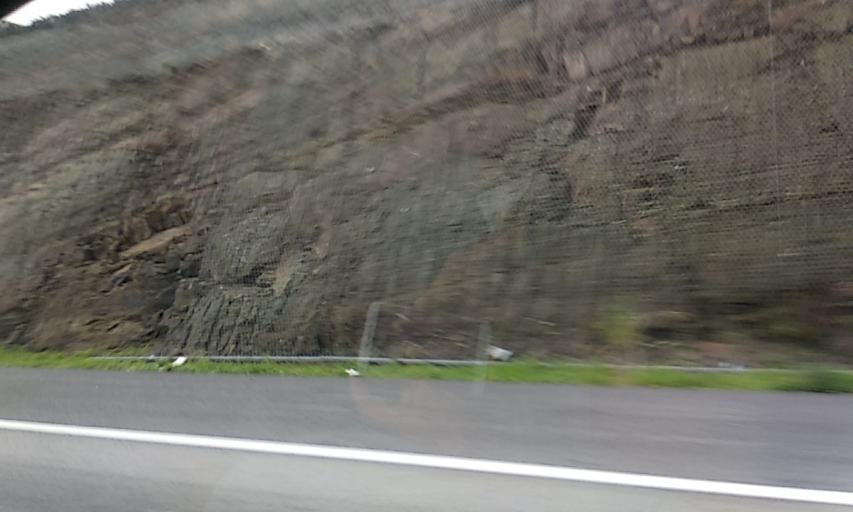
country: PT
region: Porto
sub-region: Trofa
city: Bougado
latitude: 41.3230
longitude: -8.5177
